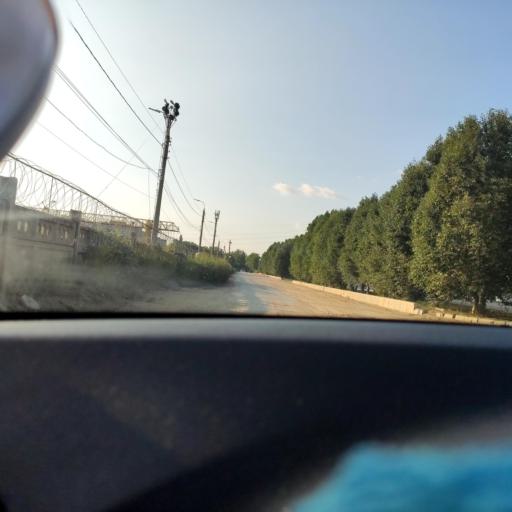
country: RU
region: Samara
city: Samara
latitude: 53.1833
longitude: 50.2623
